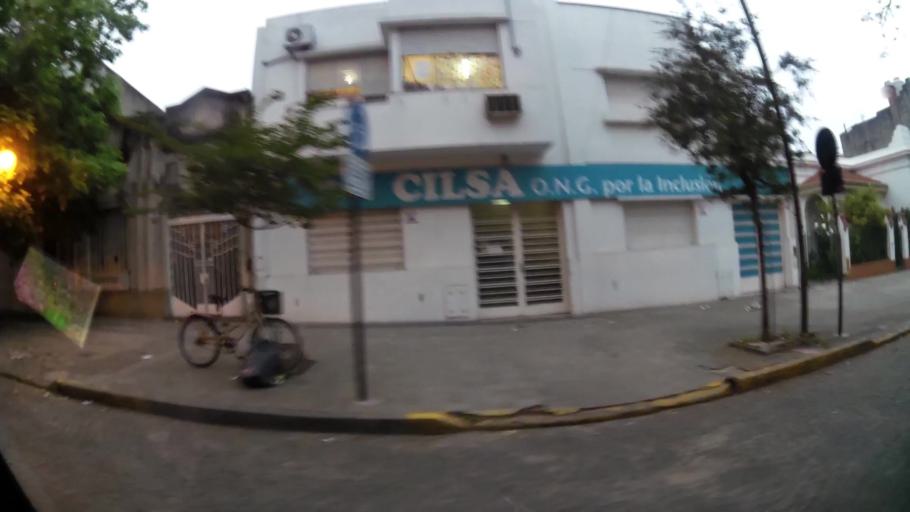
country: AR
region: Buenos Aires
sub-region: Partido de La Plata
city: La Plata
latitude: -34.9216
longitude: -57.9578
